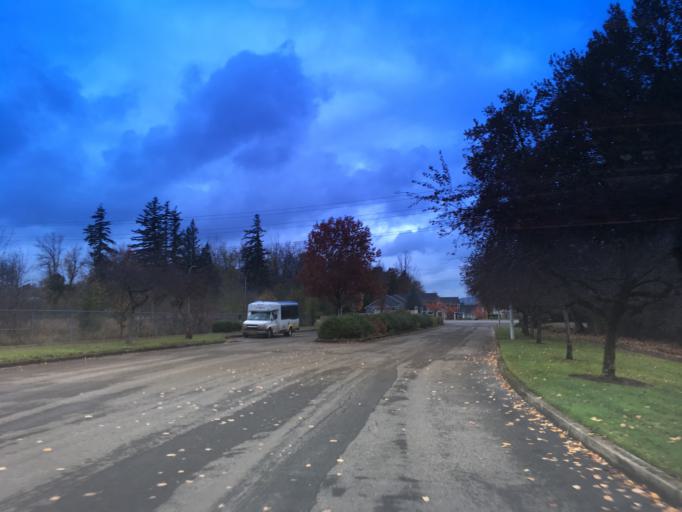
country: US
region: Oregon
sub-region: Multnomah County
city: Fairview
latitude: 45.5268
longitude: -122.4373
